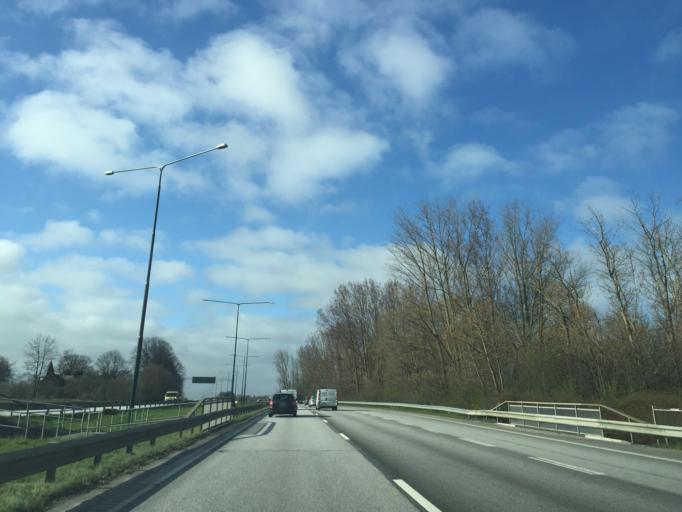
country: SE
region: Skane
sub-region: Burlovs Kommun
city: Arloev
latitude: 55.5788
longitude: 13.0522
